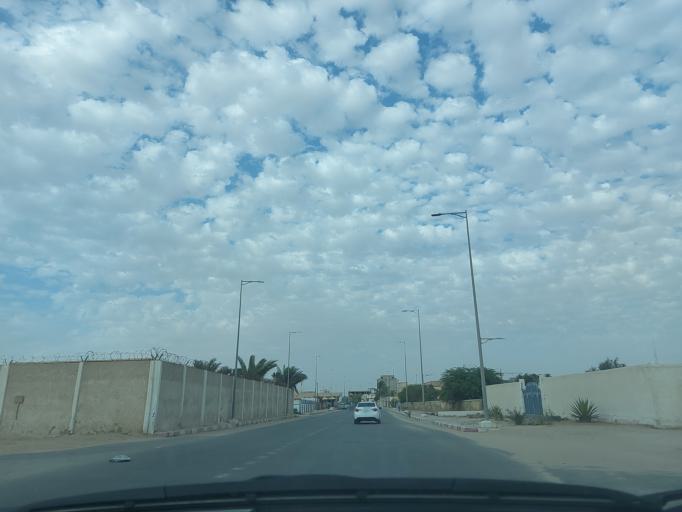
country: MR
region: Nouakchott
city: Nouakchott
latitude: 18.1092
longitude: -15.9954
